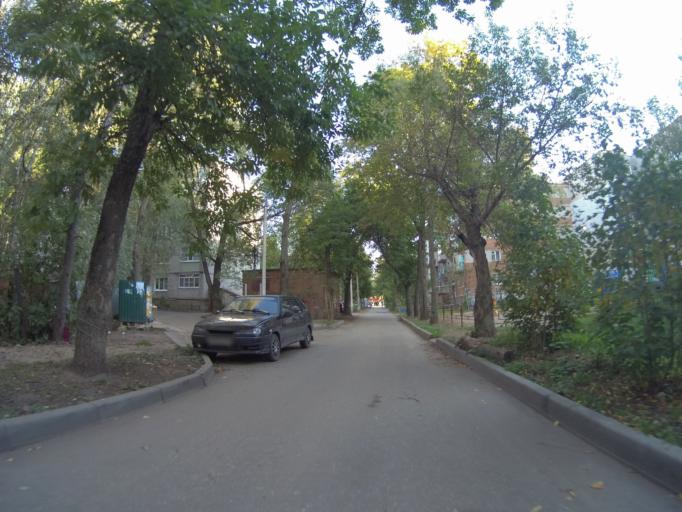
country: RU
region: Vladimir
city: Vladimir
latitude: 56.1119
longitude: 40.3479
